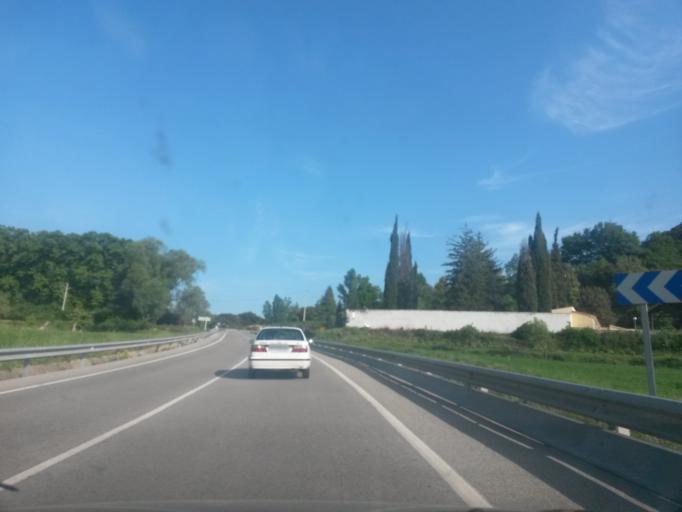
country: ES
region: Catalonia
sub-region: Provincia de Girona
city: les Planes d'Hostoles
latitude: 42.0612
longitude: 2.5351
